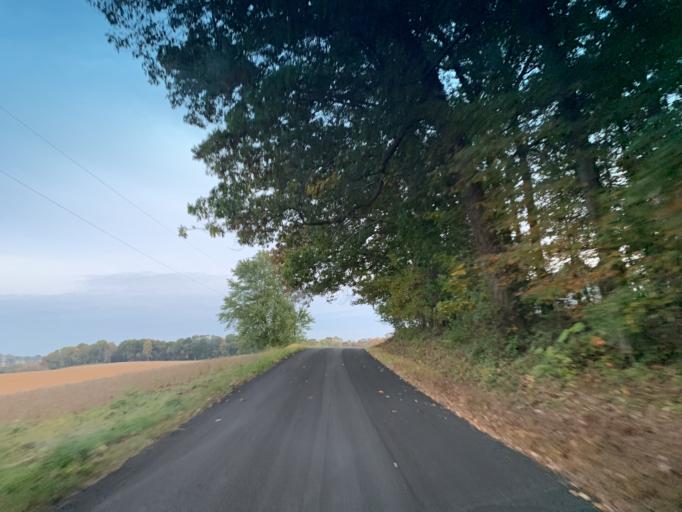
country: US
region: Pennsylvania
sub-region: York County
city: Stewartstown
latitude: 39.6671
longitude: -76.6294
